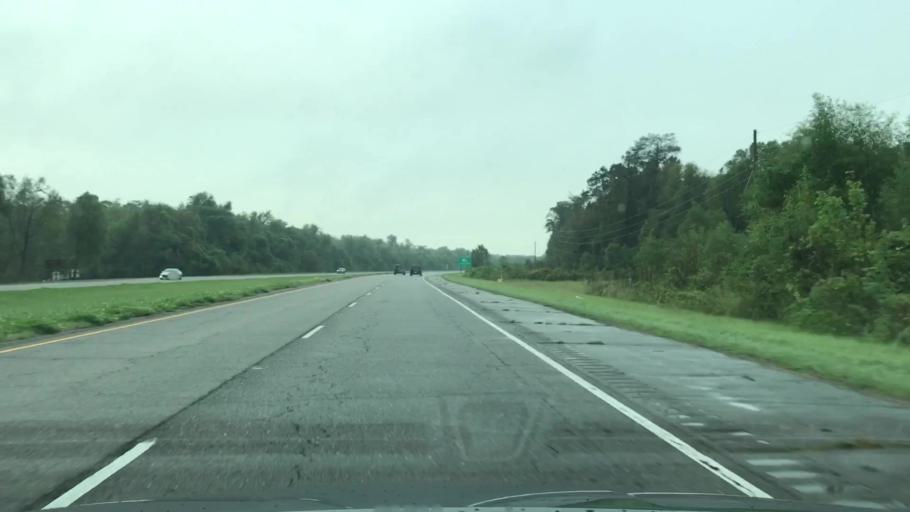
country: US
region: Louisiana
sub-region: Lafourche Parish
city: Raceland
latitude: 29.7261
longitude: -90.5593
